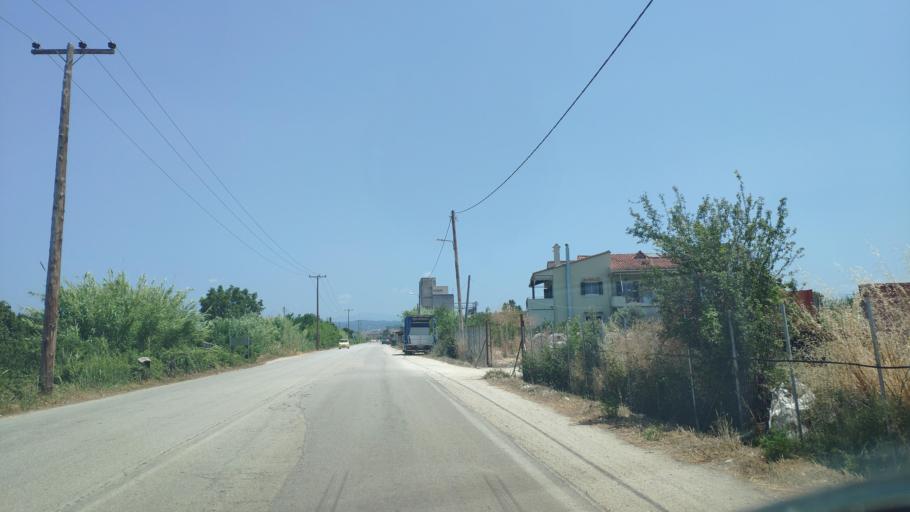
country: GR
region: Epirus
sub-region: Nomos Artas
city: Kostakioi
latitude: 39.1261
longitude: 20.9432
